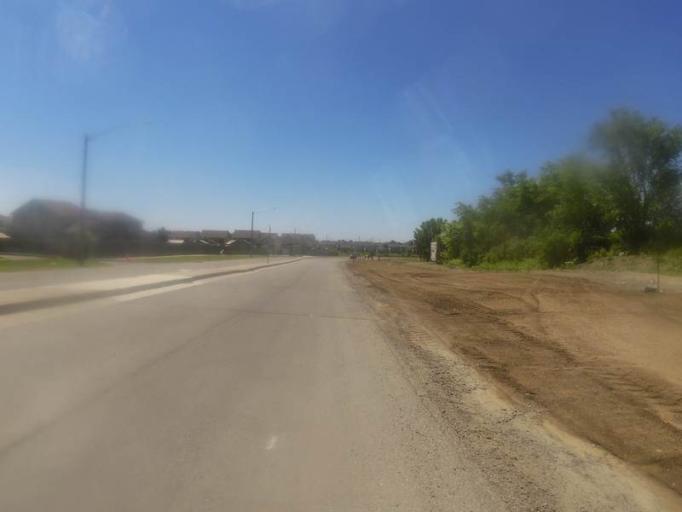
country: CA
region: Ontario
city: Kingston
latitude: 44.2690
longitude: -76.5591
